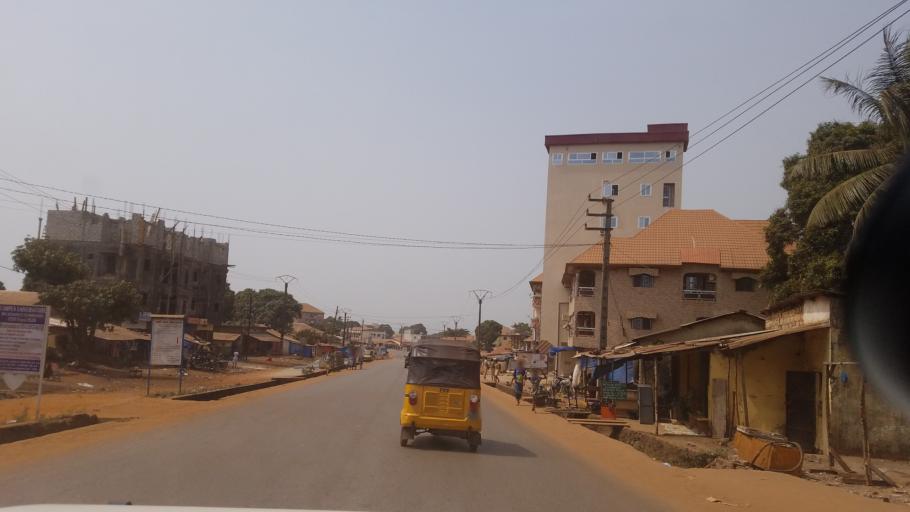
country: GN
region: Kindia
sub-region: Prefecture de Dubreka
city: Dubreka
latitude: 9.6802
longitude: -13.5689
